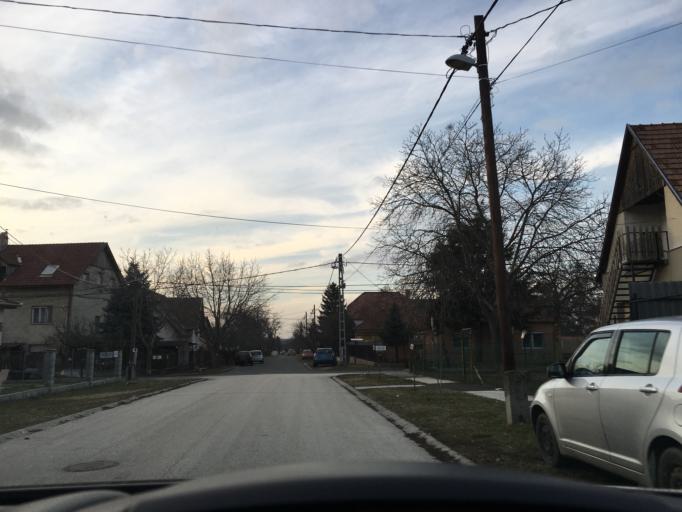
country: HU
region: Budapest
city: Budapest XVII. keruelet
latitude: 47.4744
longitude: 19.2798
